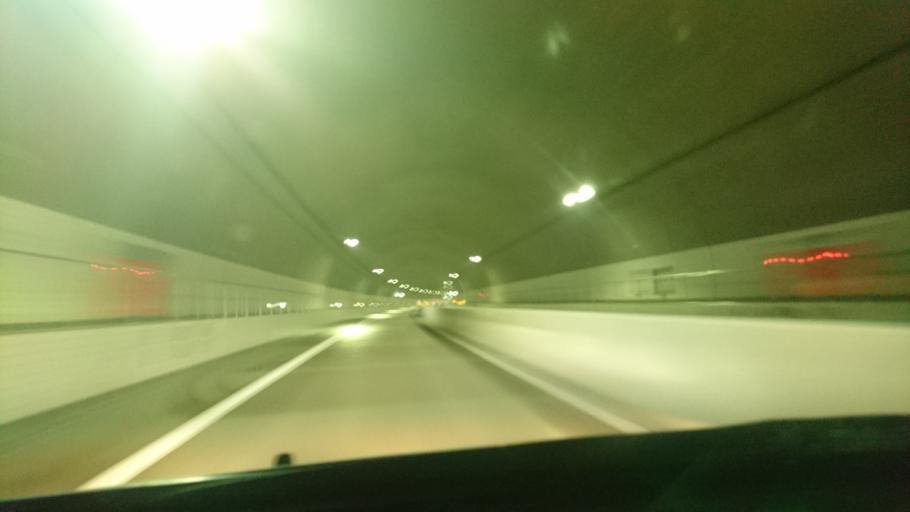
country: JP
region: Iwate
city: Miyako
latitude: 39.8121
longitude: 141.9581
